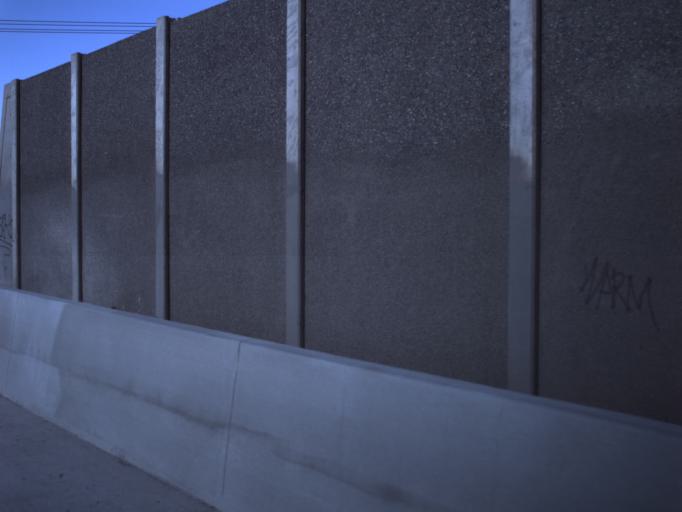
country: US
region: Utah
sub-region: Salt Lake County
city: Taylorsville
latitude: 40.6890
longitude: -111.9515
